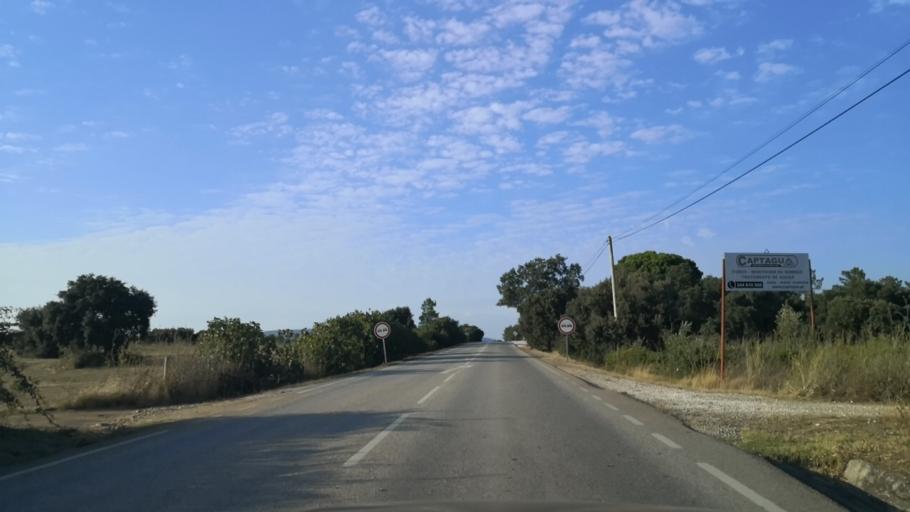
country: PT
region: Santarem
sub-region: Alcanena
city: Alcanena
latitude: 39.4225
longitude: -8.6352
